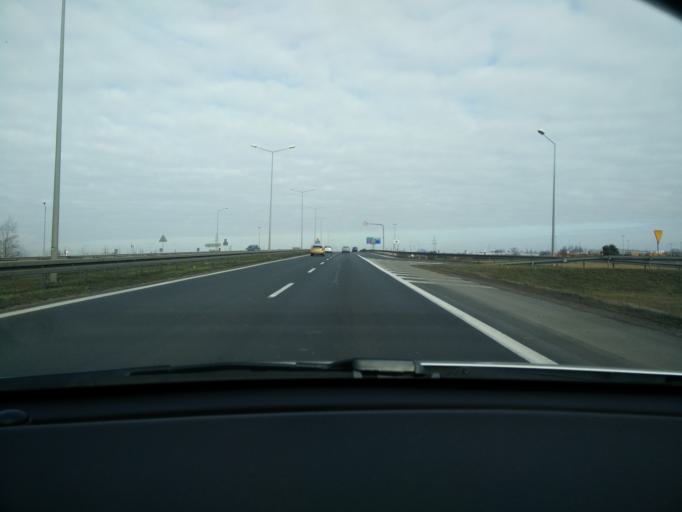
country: PL
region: Greater Poland Voivodeship
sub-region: Powiat poznanski
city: Daszewice
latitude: 52.3439
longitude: 17.0001
